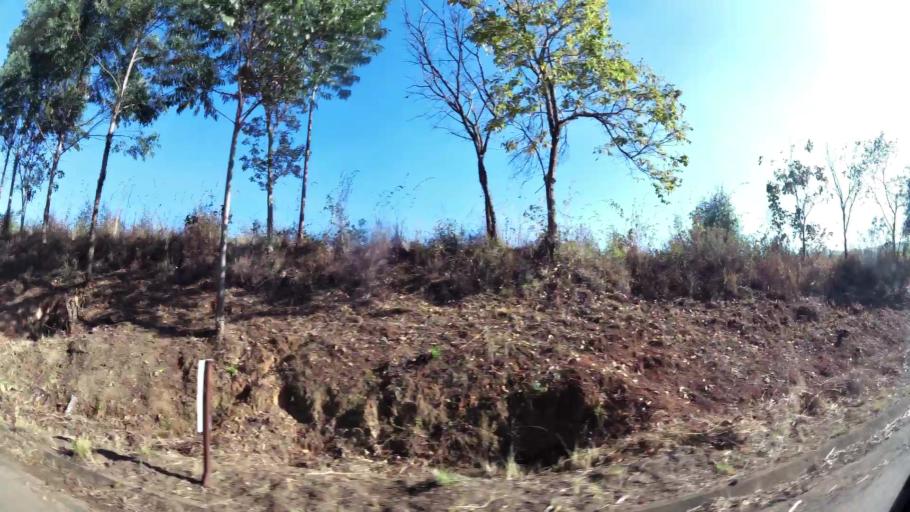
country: ZA
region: Limpopo
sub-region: Mopani District Municipality
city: Tzaneen
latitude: -23.8823
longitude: 30.0876
